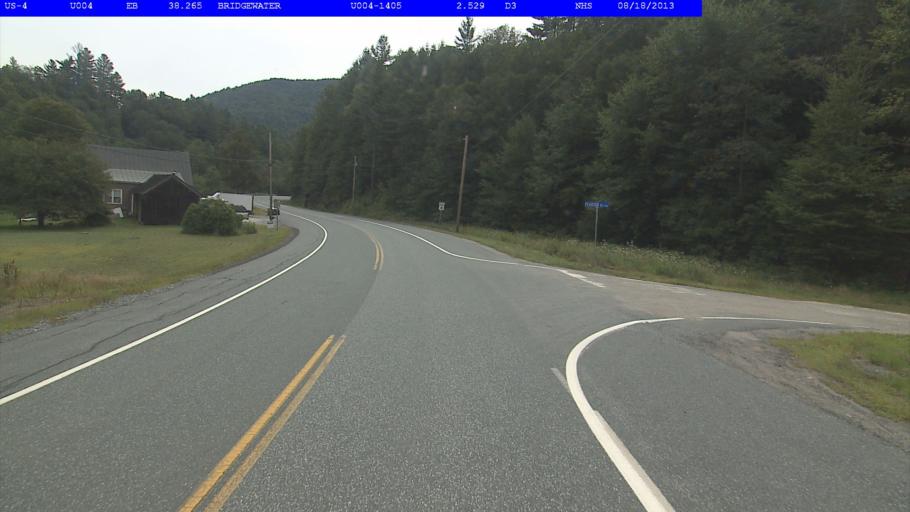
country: US
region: Vermont
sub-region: Windsor County
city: Woodstock
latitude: 43.5943
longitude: -72.7083
